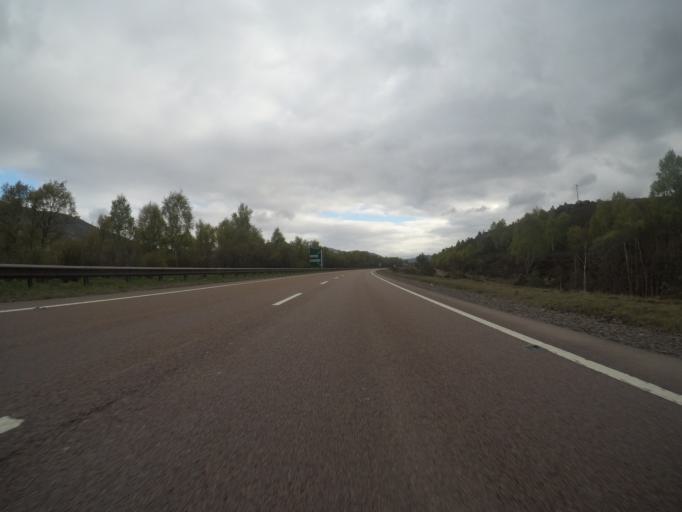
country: GB
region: Scotland
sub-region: Highland
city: Kingussie
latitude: 57.0411
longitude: -4.1489
